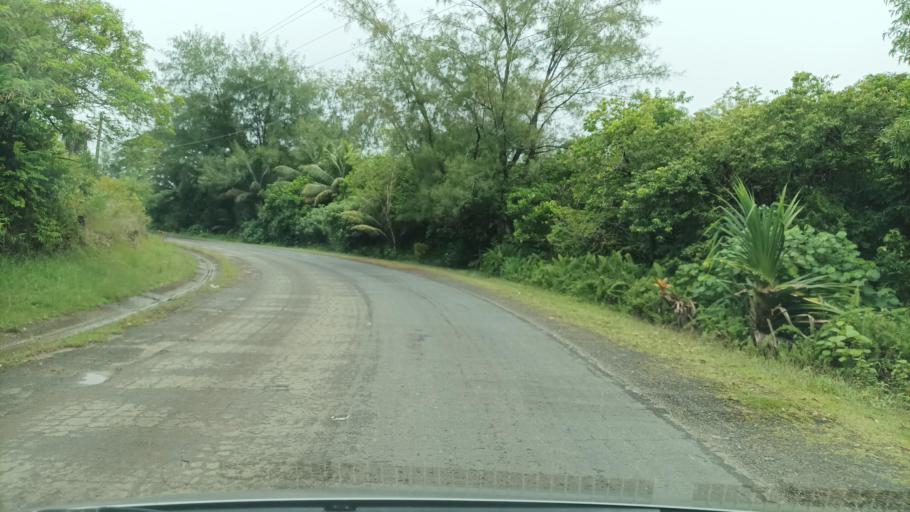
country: FM
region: Yap
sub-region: Weloy Municipality
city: Colonia
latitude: 9.5479
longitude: 138.1588
